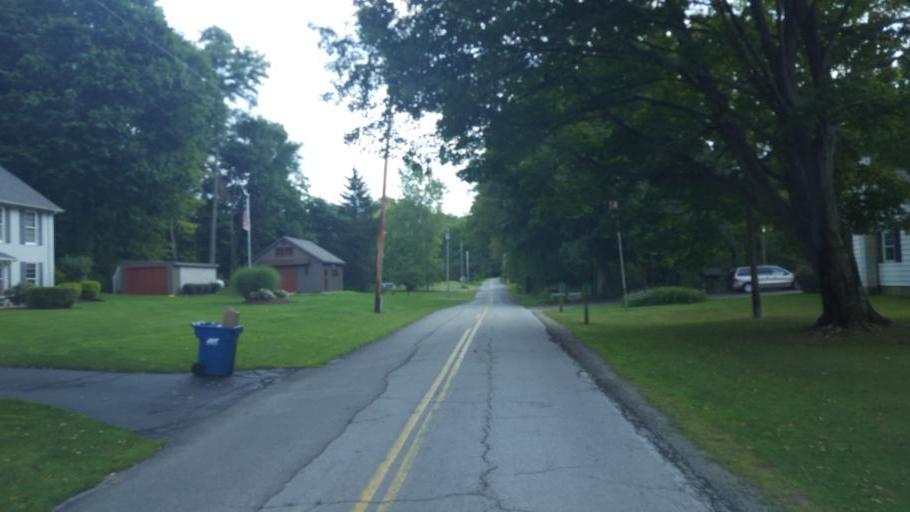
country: US
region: Ohio
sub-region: Huron County
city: Norwalk
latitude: 41.1690
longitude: -82.6422
